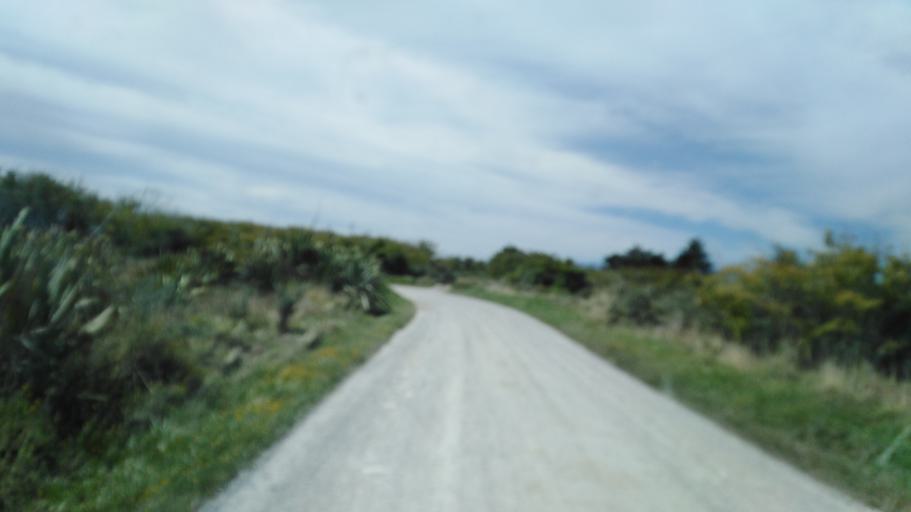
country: NZ
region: West Coast
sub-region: Buller District
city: Westport
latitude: -41.7363
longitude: 171.6048
